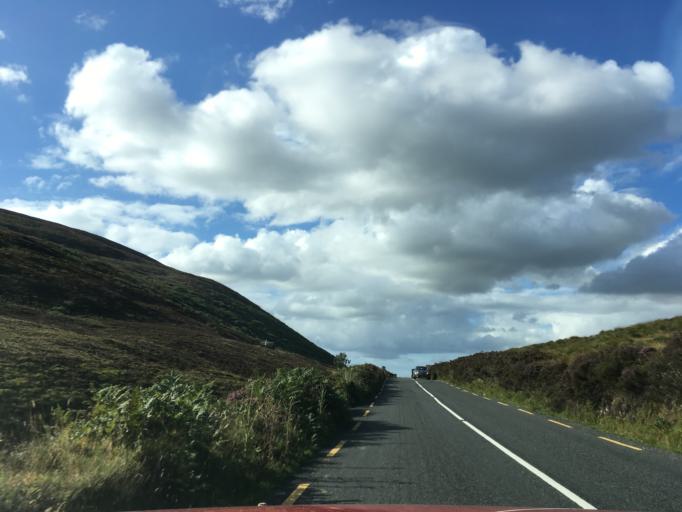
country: IE
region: Munster
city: Cahir
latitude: 52.2395
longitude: -7.9548
